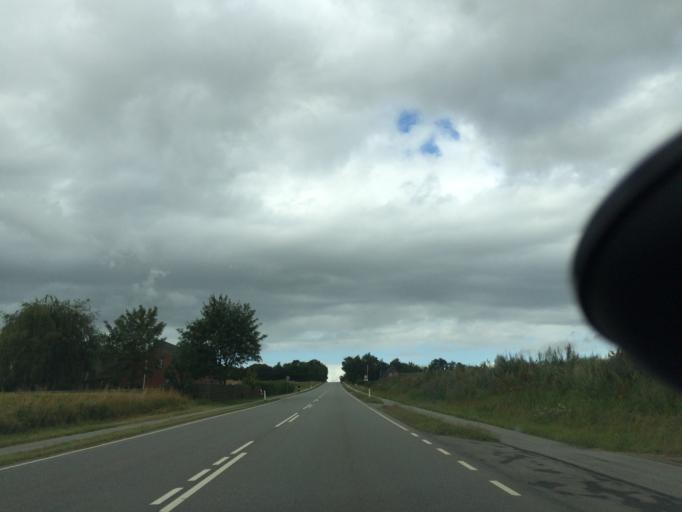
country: DK
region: Central Jutland
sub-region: Skanderborg Kommune
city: Galten
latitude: 56.1483
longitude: 9.8879
